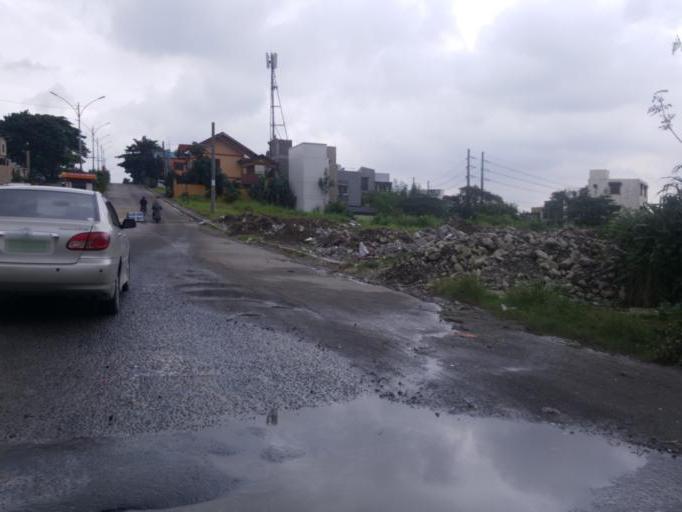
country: PH
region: Calabarzon
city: Bagong Pagasa
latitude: 14.7126
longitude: 121.0209
